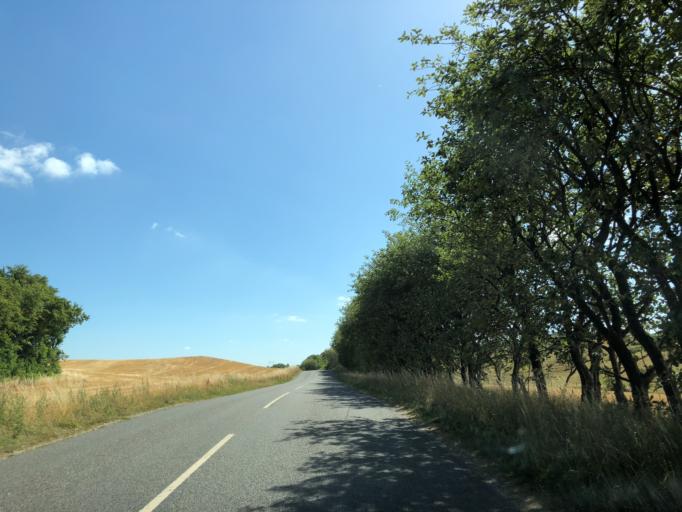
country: DK
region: North Denmark
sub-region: Vesthimmerland Kommune
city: Alestrup
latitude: 56.5761
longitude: 9.5280
